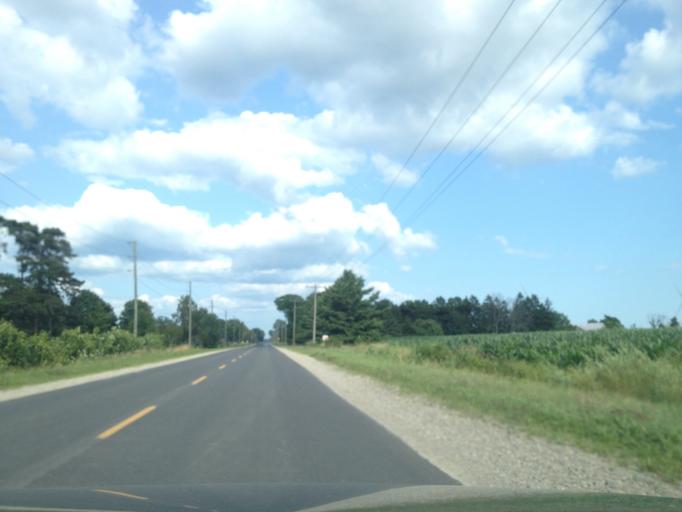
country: CA
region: Ontario
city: Aylmer
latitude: 42.6741
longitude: -80.8906
